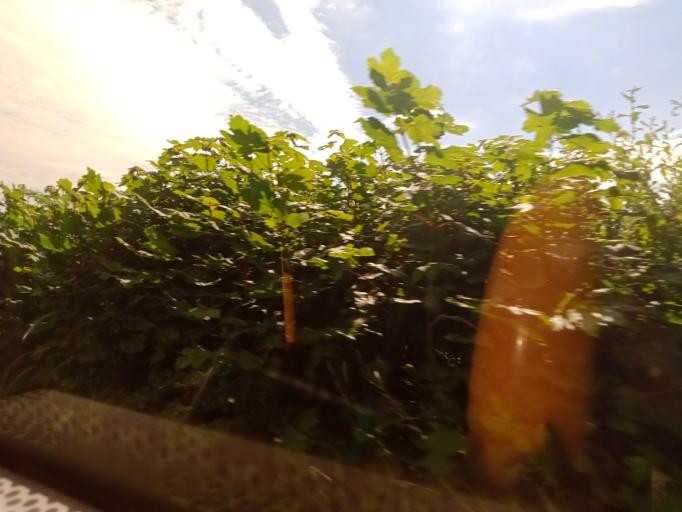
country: GB
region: Wales
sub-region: Anglesey
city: Llangoed
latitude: 53.2984
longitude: -4.0835
